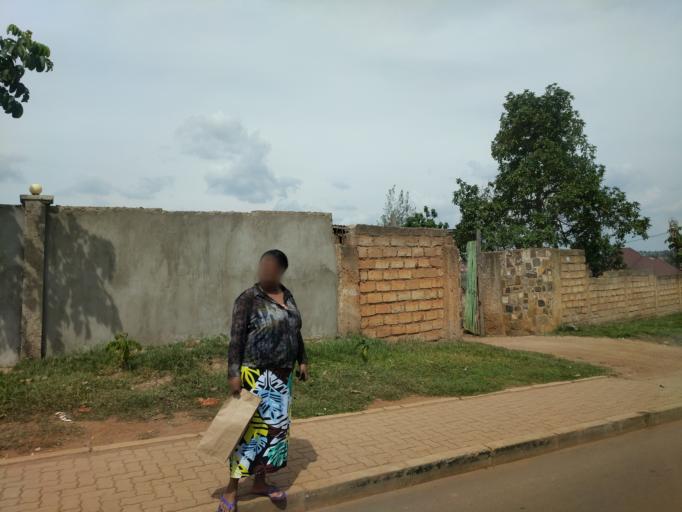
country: RW
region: Kigali
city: Kigali
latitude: -1.9830
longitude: 30.1191
